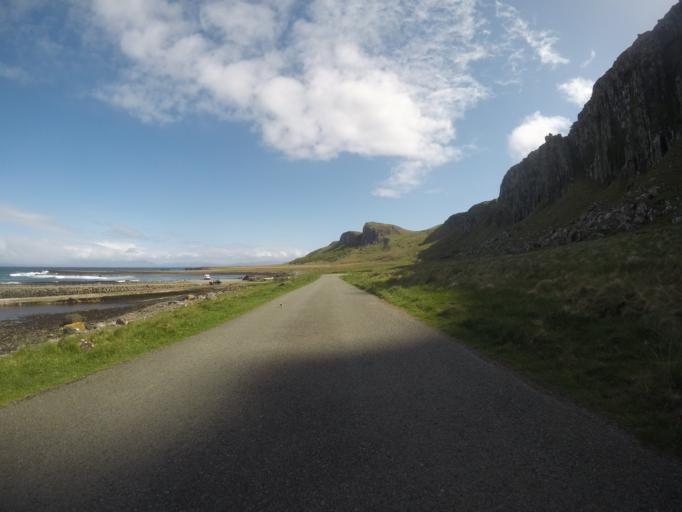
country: GB
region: Scotland
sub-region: Highland
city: Portree
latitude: 57.6336
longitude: -6.2005
